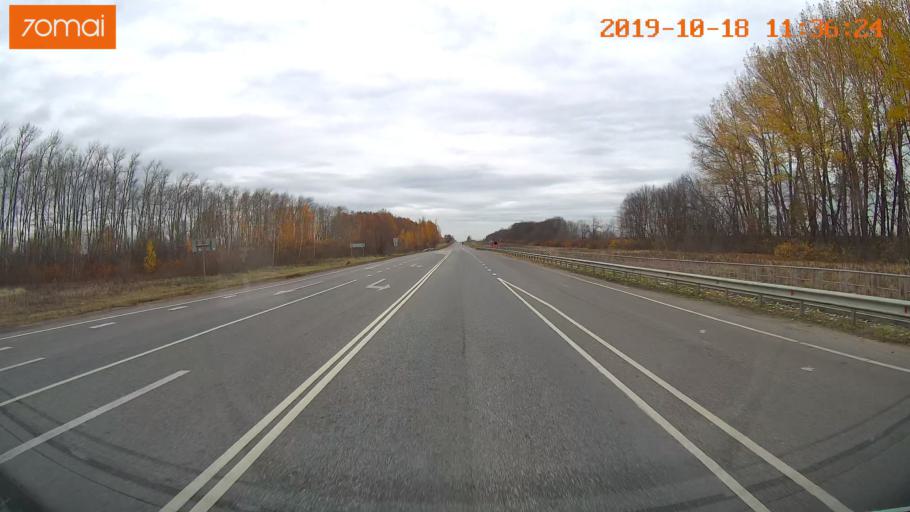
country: RU
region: Rjazan
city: Oktyabr'skiy
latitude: 54.1402
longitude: 38.8056
